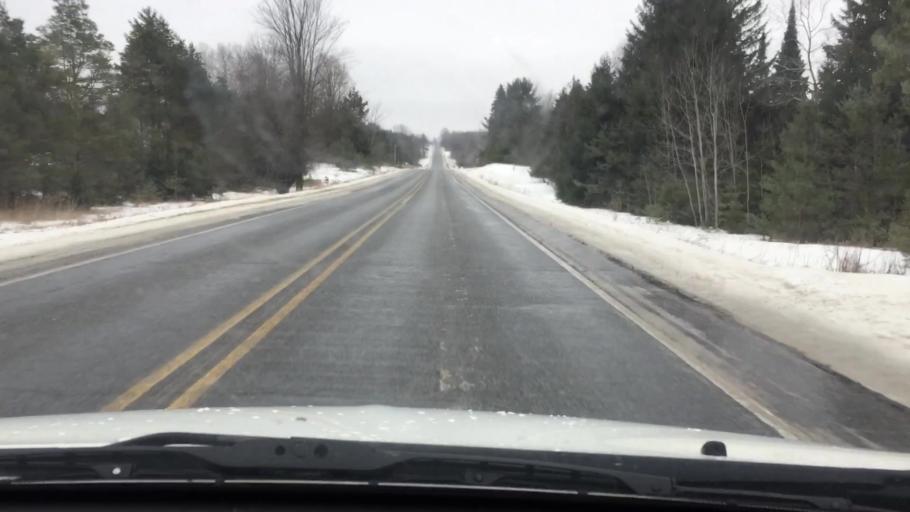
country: US
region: Michigan
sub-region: Wexford County
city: Cadillac
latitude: 44.0911
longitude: -85.4442
